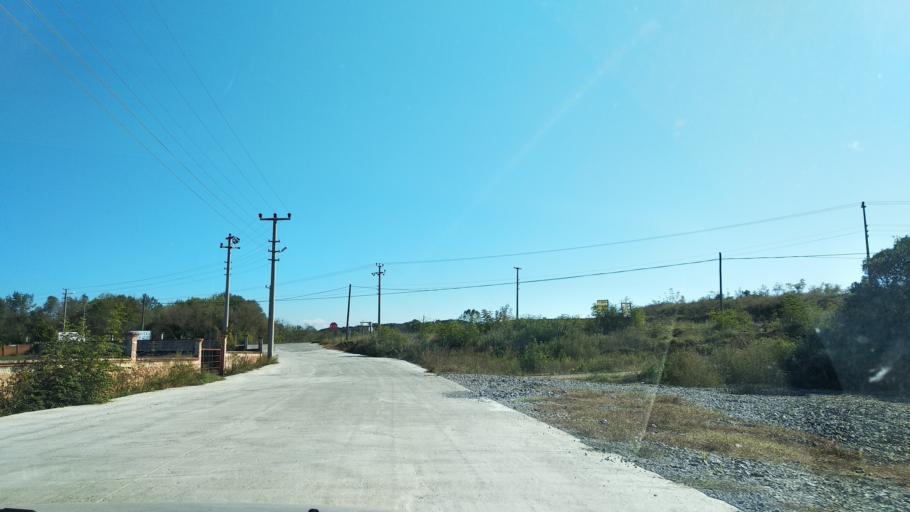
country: TR
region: Sakarya
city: Karasu
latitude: 41.1196
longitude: 30.6081
